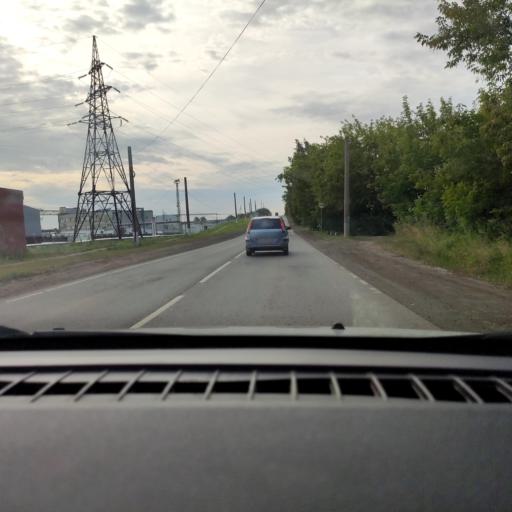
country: RU
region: Perm
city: Gamovo
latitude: 57.9128
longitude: 56.1574
